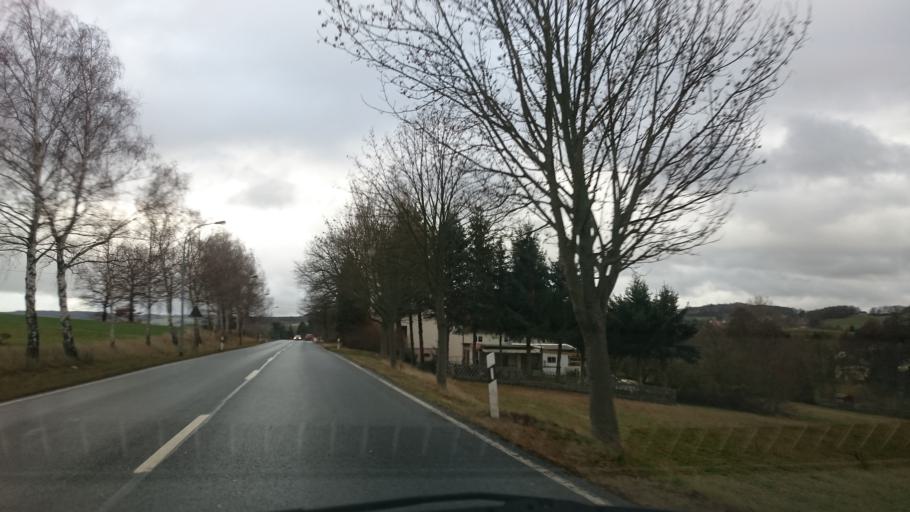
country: DE
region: Saxony
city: Kirchberg
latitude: 50.6540
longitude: 12.5580
